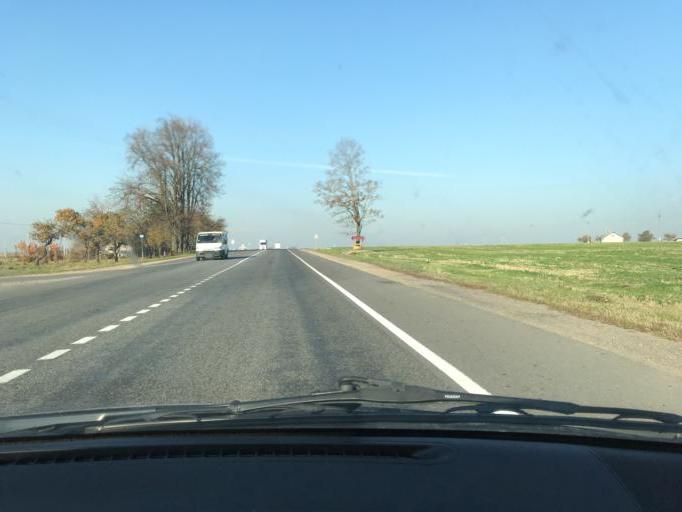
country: BY
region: Mogilev
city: Shklow
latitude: 54.2336
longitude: 30.4517
